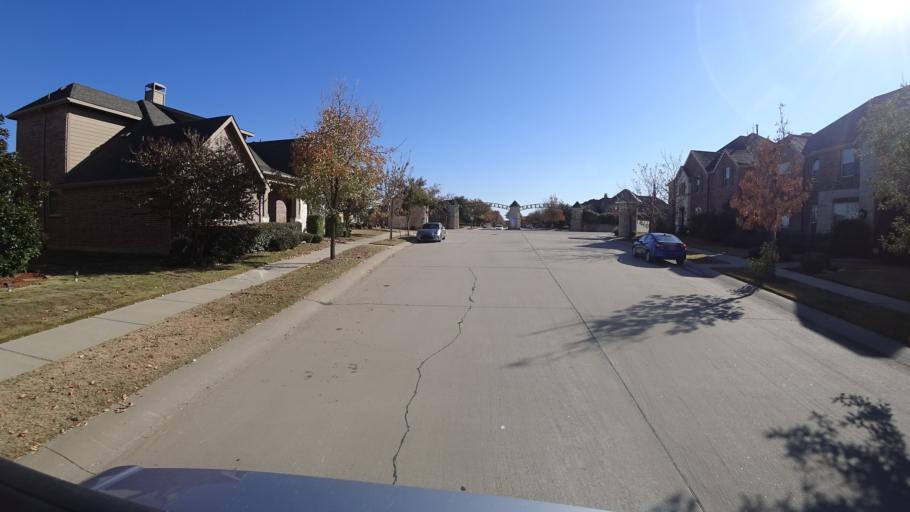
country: US
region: Texas
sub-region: Denton County
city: The Colony
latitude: 33.0396
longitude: -96.9191
